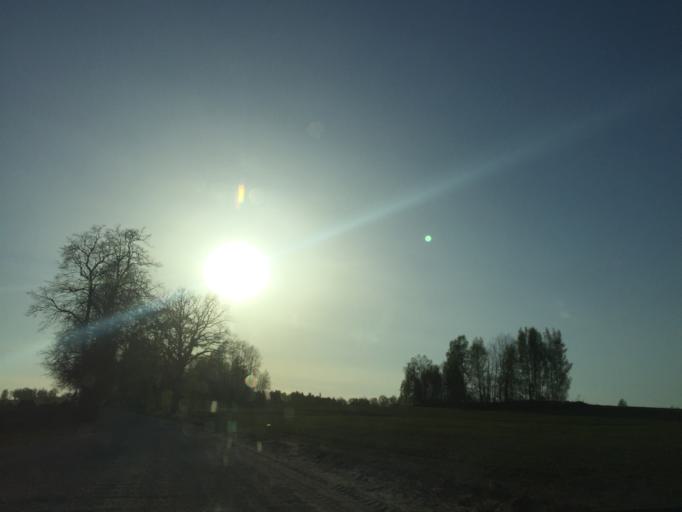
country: LV
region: Ergli
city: Ergli
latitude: 56.7385
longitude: 25.5858
